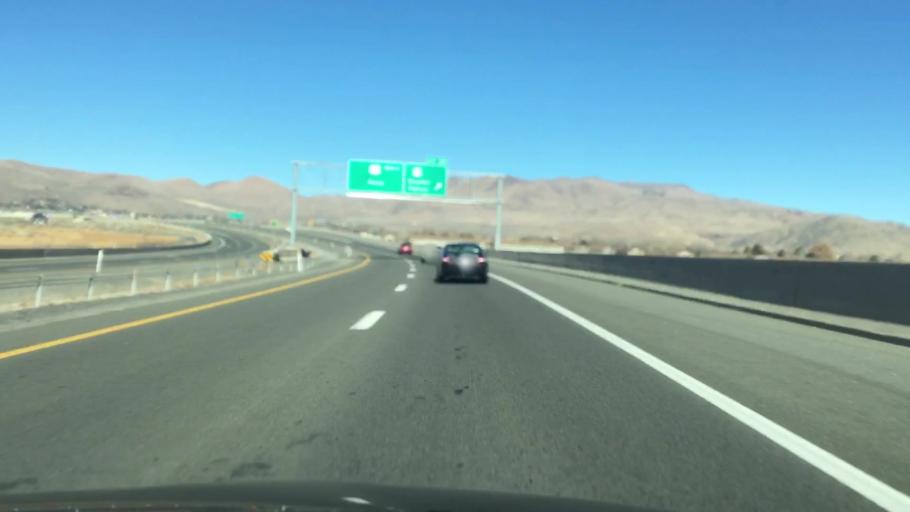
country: US
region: Nevada
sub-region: Carson City
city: Carson City
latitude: 39.1678
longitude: -119.7380
